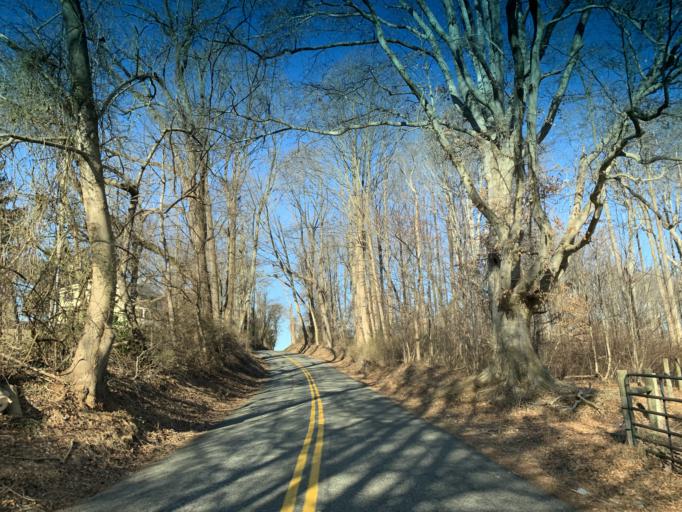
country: US
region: Maryland
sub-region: Harford County
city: Aberdeen
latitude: 39.5885
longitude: -76.2159
